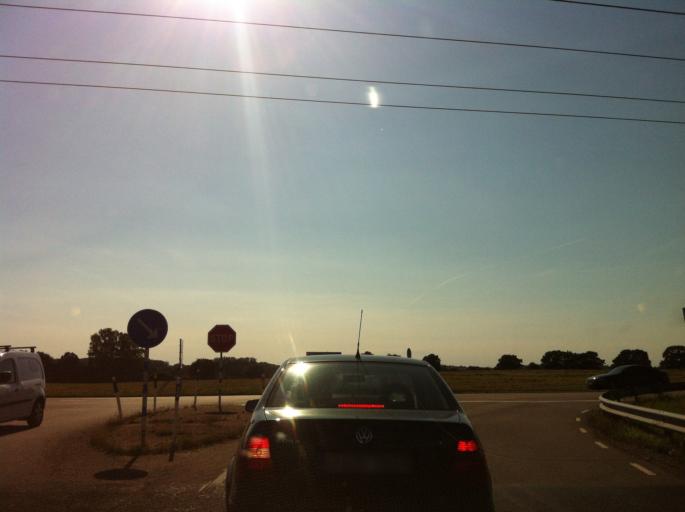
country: SE
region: Skane
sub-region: Astorps Kommun
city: Astorp
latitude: 56.0977
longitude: 12.9709
